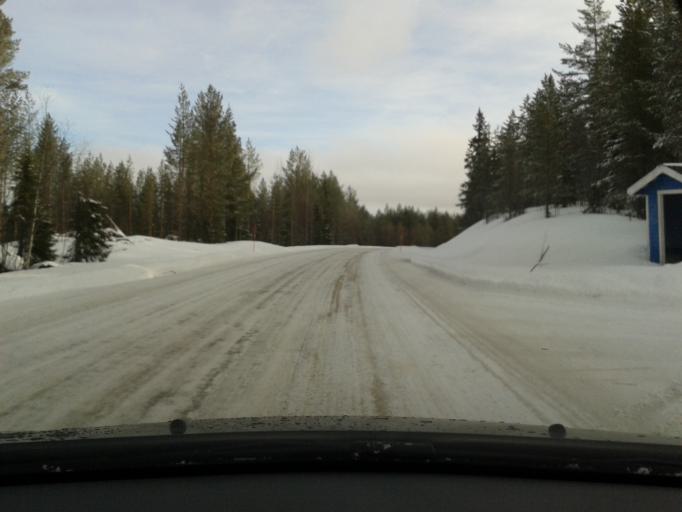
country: SE
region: Vaesterbotten
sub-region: Vilhelmina Kommun
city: Sjoberg
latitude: 64.7986
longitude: 16.0414
